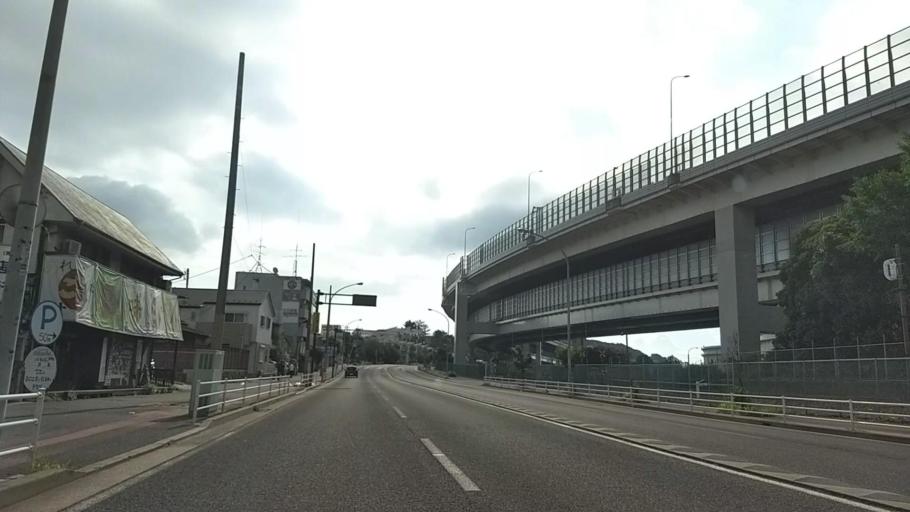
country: JP
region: Kanagawa
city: Yokohama
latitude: 35.4187
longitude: 139.6458
